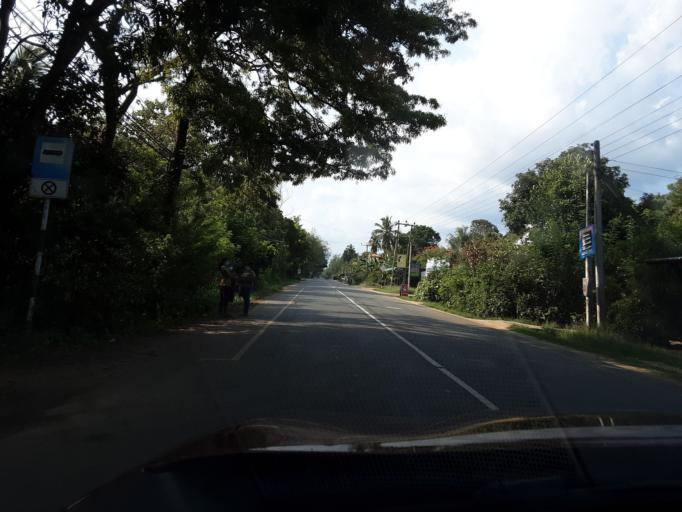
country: LK
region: Uva
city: Haputale
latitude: 6.6604
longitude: 81.1146
